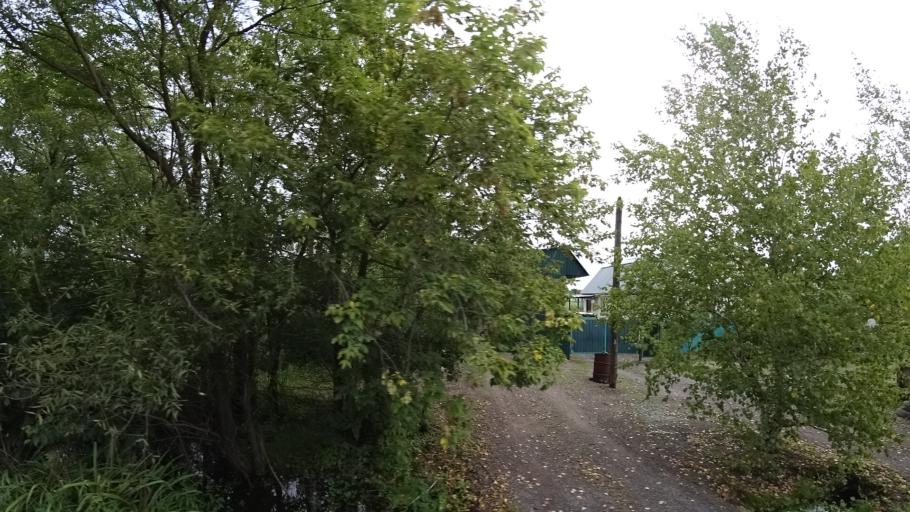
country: RU
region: Primorskiy
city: Chernigovka
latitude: 44.3439
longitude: 132.5615
